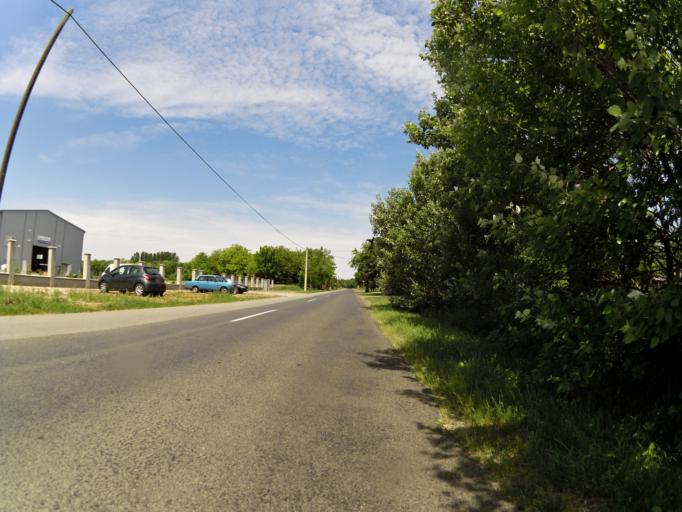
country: HU
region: Csongrad
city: Sandorfalva
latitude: 46.4188
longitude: 20.1124
